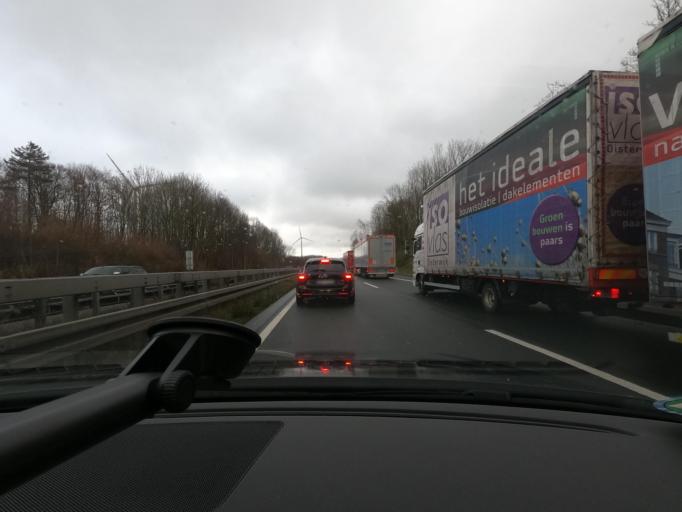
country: DE
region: North Rhine-Westphalia
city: Marsberg
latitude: 51.5518
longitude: 8.8084
